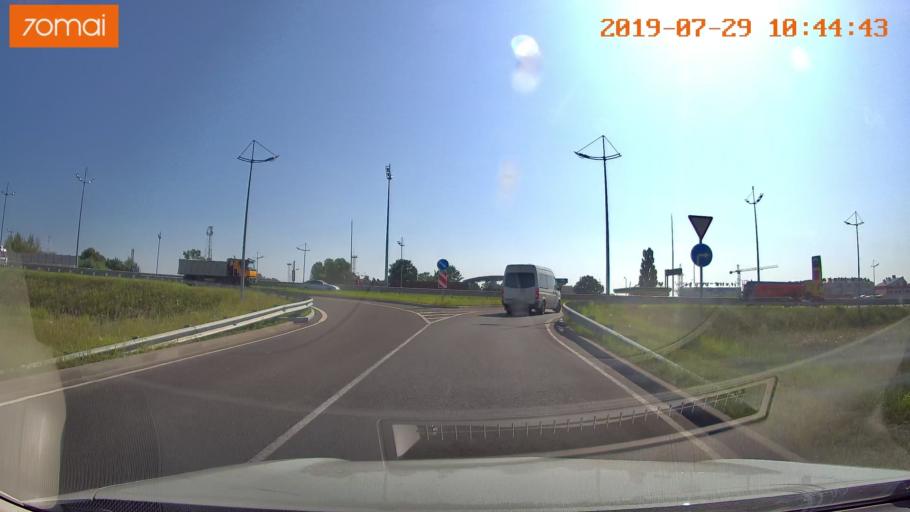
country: RU
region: Kaliningrad
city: Bol'shoe Isakovo
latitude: 54.7145
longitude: 20.5944
